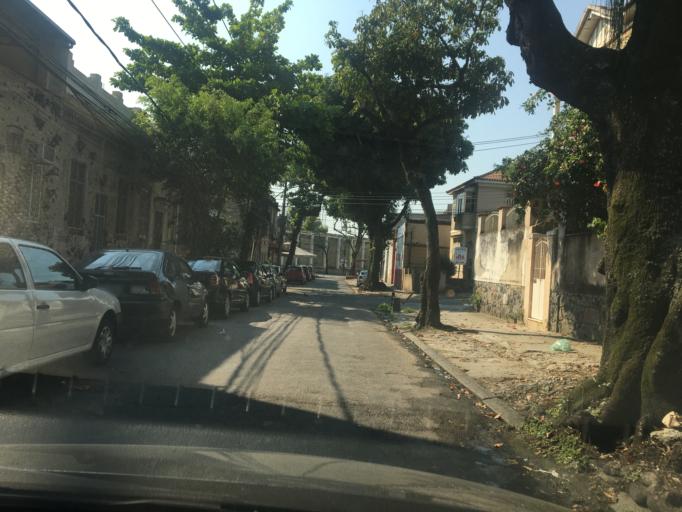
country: BR
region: Rio de Janeiro
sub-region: Rio De Janeiro
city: Rio de Janeiro
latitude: -22.8928
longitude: -43.2269
